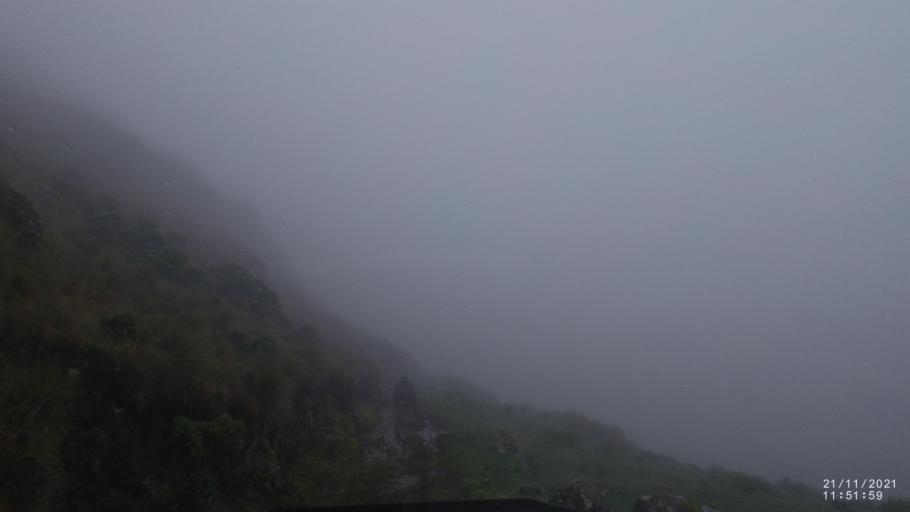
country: BO
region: Cochabamba
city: Cochabamba
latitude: -16.9460
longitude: -66.2560
